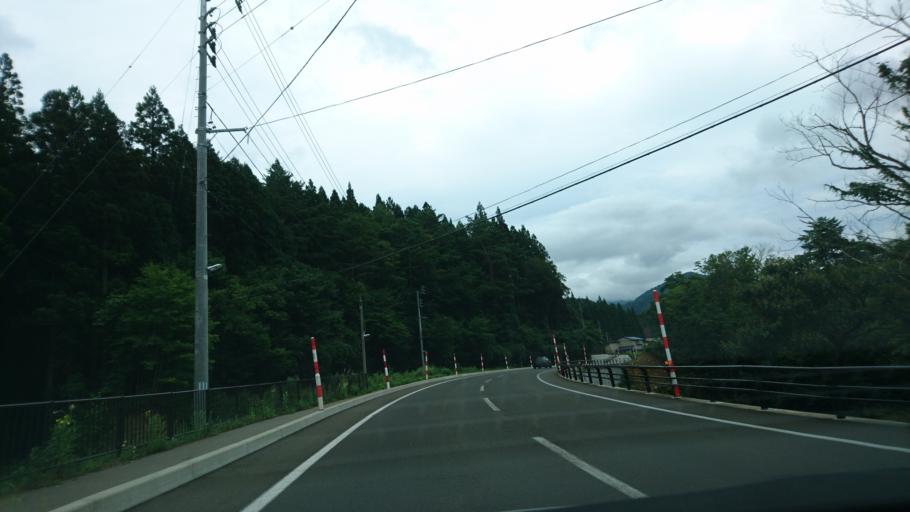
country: JP
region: Akita
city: Yuzawa
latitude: 38.9580
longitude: 140.5386
